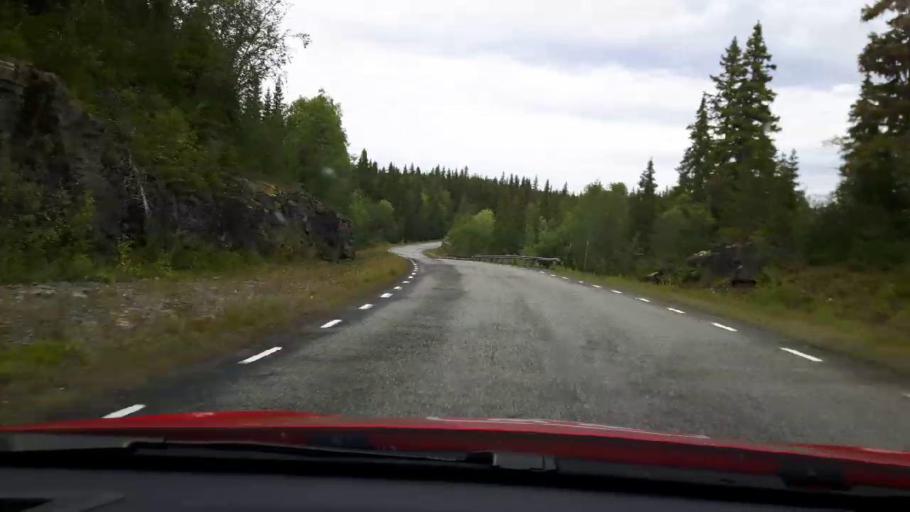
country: SE
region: Jaemtland
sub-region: Are Kommun
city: Are
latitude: 63.7046
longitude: 12.9503
